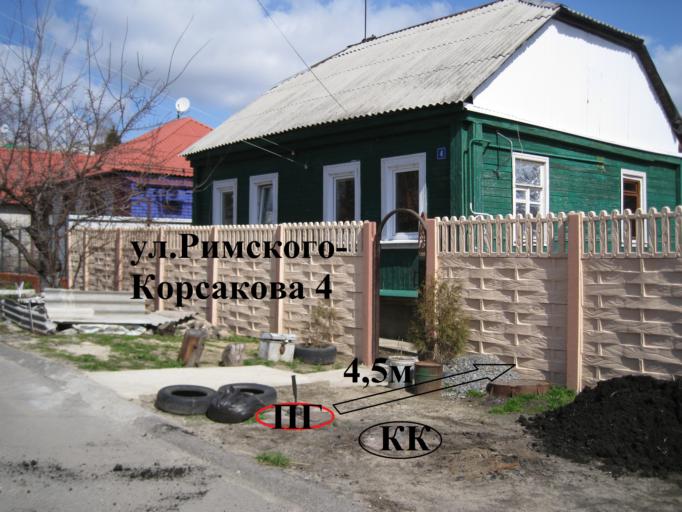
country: RU
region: Voronezj
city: Voronezh
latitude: 51.6315
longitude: 39.1943
